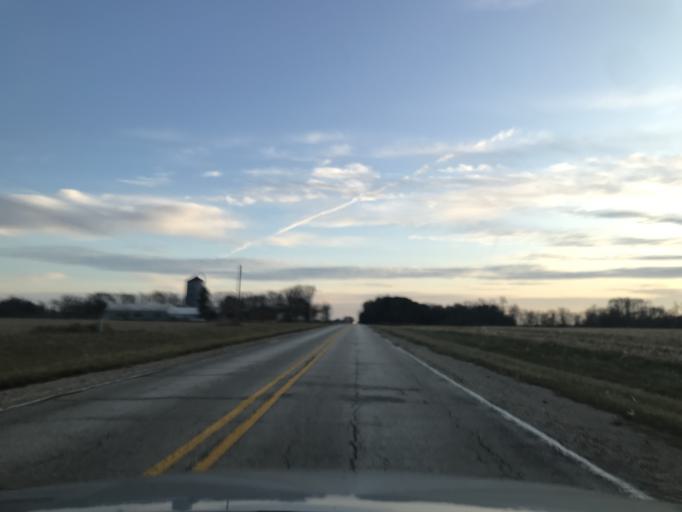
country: US
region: Illinois
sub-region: Henderson County
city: Oquawka
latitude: 40.9566
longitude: -90.8641
